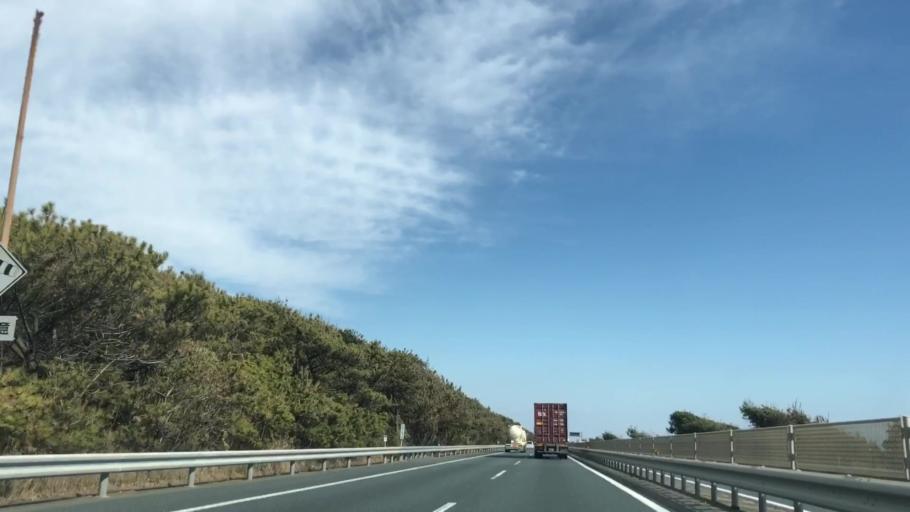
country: JP
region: Shizuoka
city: Kosai-shi
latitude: 34.6797
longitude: 137.5426
